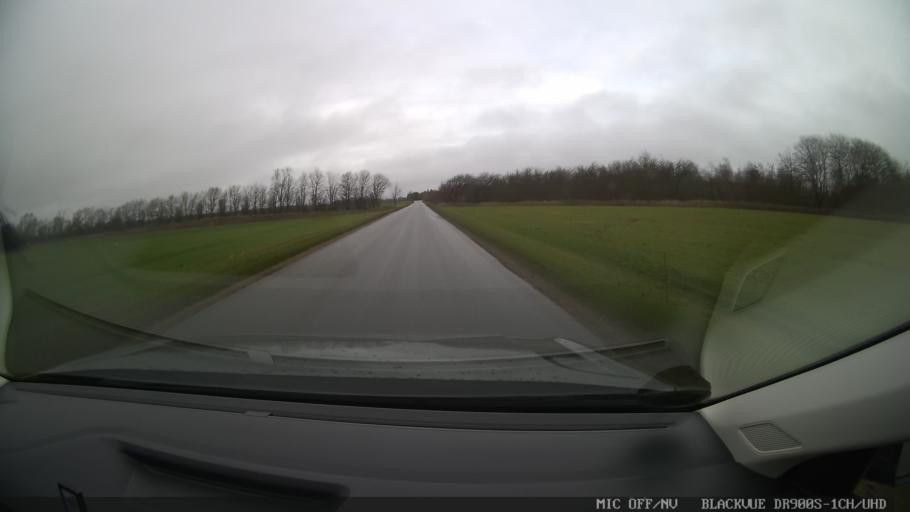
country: DK
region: Central Jutland
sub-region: Viborg Kommune
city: Karup
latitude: 56.3411
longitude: 9.2788
